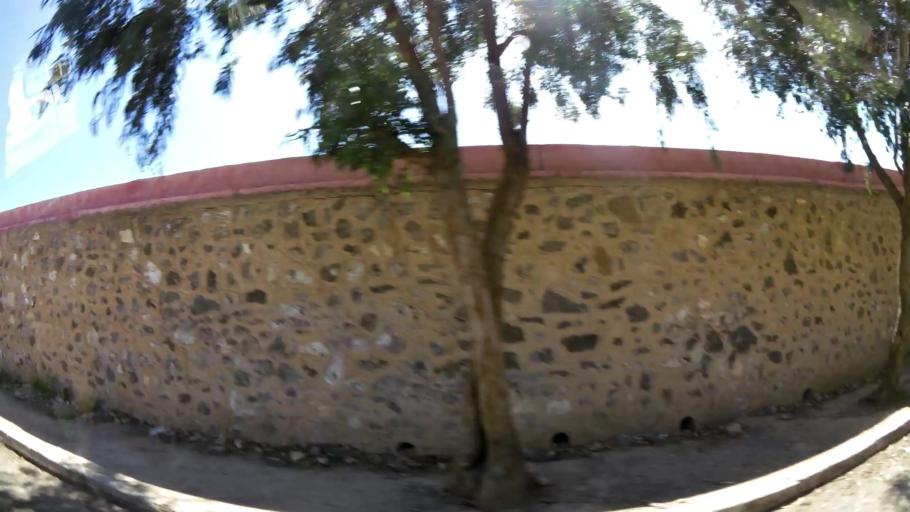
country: MA
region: Oriental
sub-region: Oujda-Angad
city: Oujda
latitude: 34.6508
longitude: -1.9087
